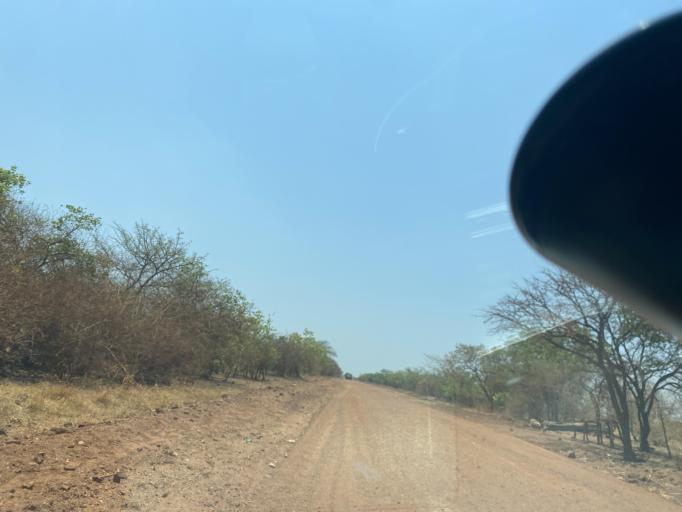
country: ZM
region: Lusaka
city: Lusaka
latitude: -15.4583
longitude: 27.9330
